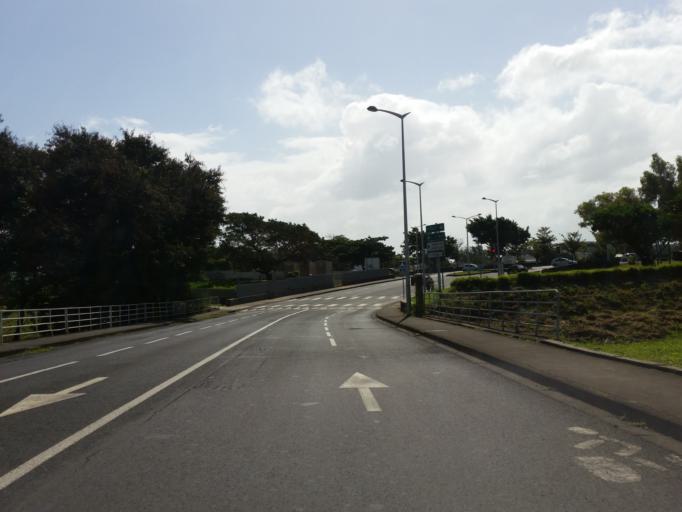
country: RE
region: Reunion
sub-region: Reunion
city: Saint-Denis
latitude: -20.8931
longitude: 55.4672
